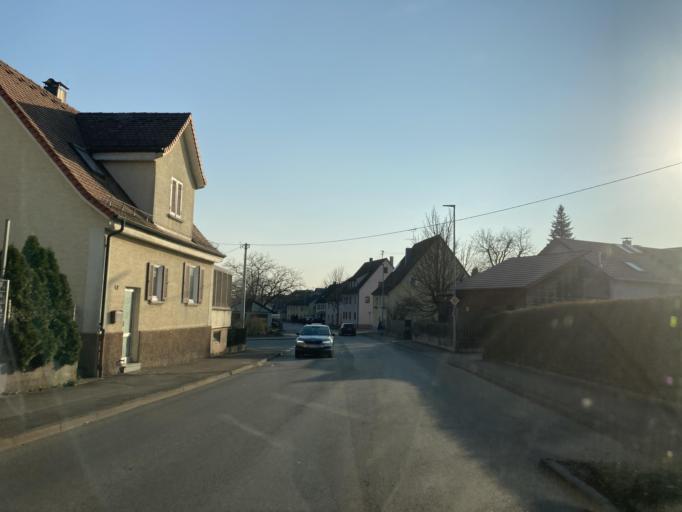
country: DE
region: Baden-Wuerttemberg
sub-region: Tuebingen Region
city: Rottenburg
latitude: 48.5056
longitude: 8.9648
